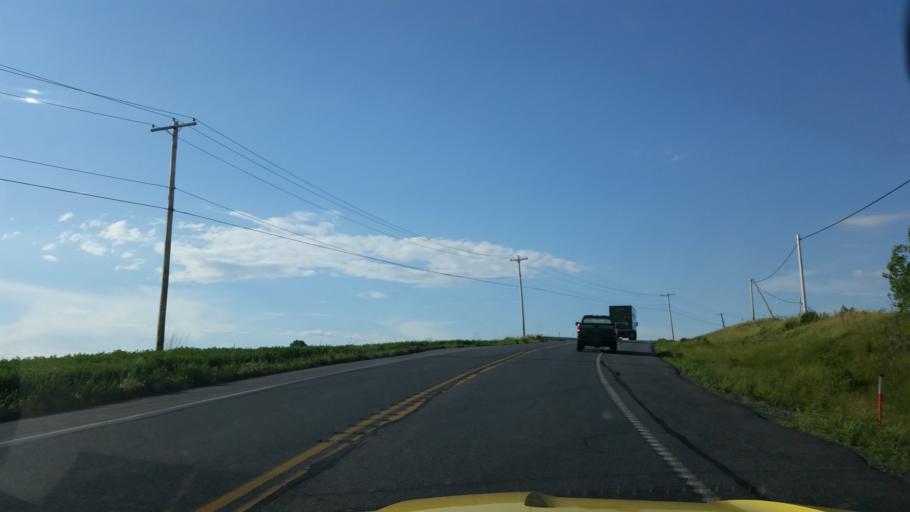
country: US
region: Pennsylvania
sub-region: Lancaster County
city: Brickerville
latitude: 40.2836
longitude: -76.3043
